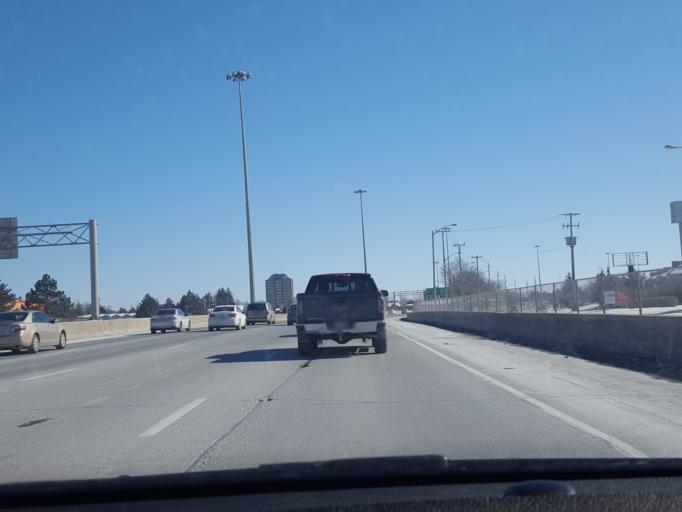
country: CA
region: Ontario
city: Kitchener
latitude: 43.4319
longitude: -80.4436
